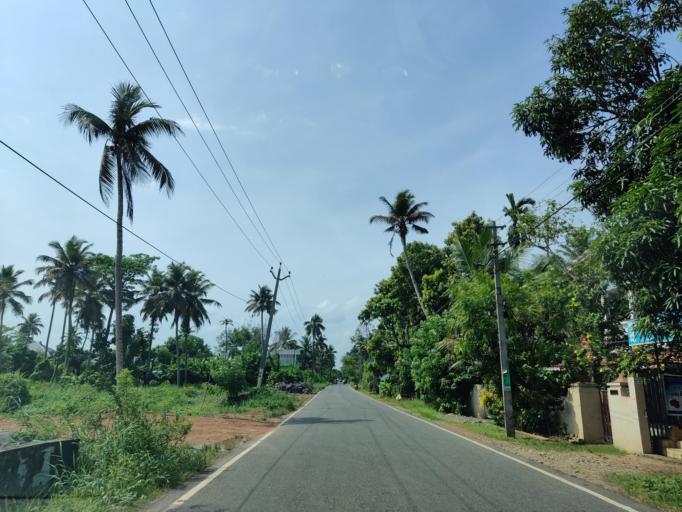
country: IN
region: Kerala
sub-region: Pattanamtitta
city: Tiruvalla
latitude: 9.3418
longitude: 76.4680
